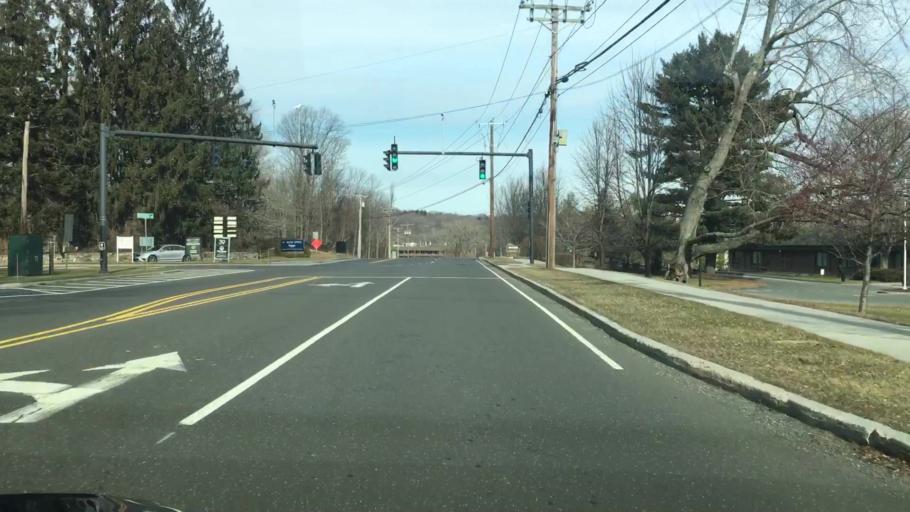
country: US
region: Connecticut
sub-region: Fairfield County
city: Danbury
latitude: 41.3849
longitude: -73.5153
